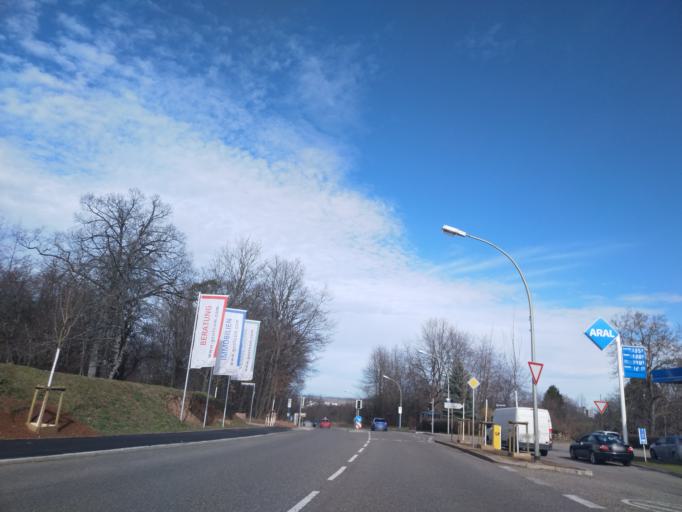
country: DE
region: Baden-Wuerttemberg
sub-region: Karlsruhe Region
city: Birkenfeld
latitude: 48.8617
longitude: 8.6616
